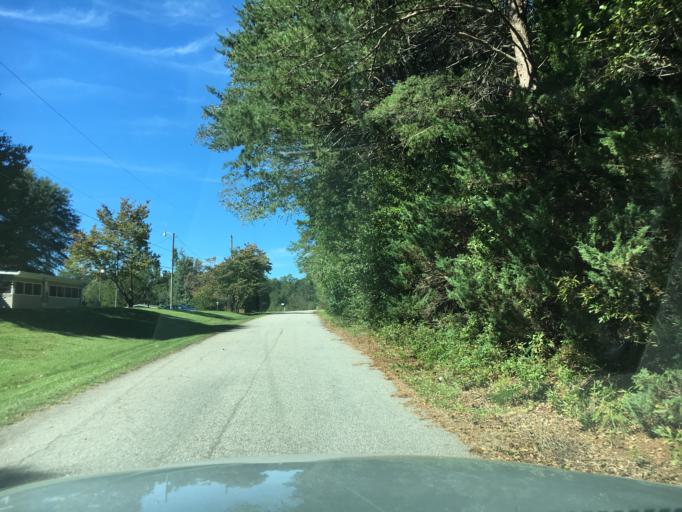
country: US
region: South Carolina
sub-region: Spartanburg County
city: Duncan
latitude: 34.9481
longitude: -82.1553
